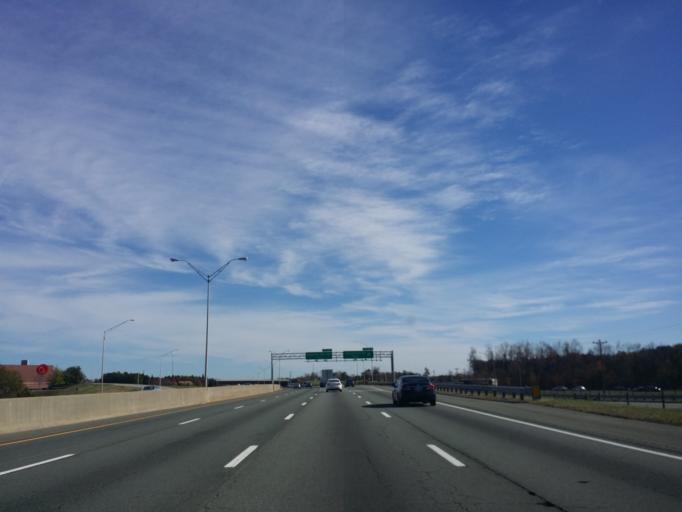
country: US
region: North Carolina
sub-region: Alamance County
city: Elon
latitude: 36.0645
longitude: -79.5223
